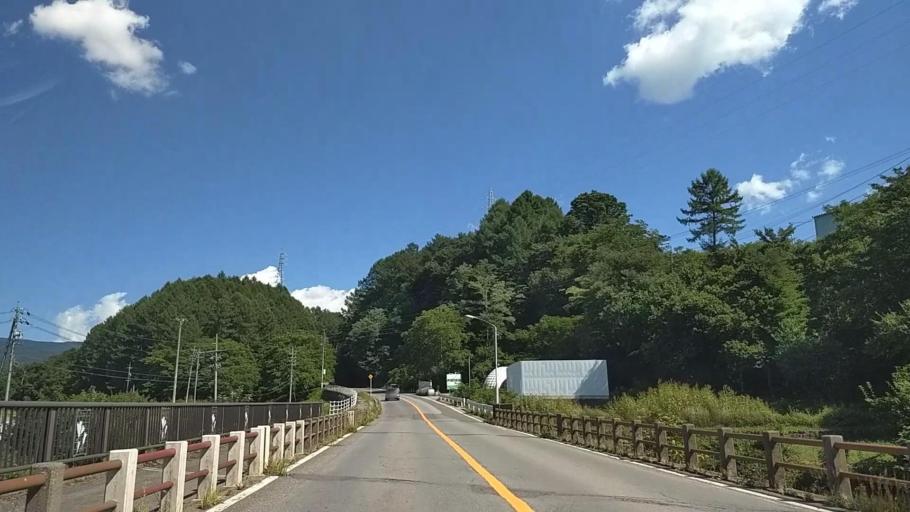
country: JP
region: Nagano
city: Chino
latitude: 36.0328
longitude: 138.2016
